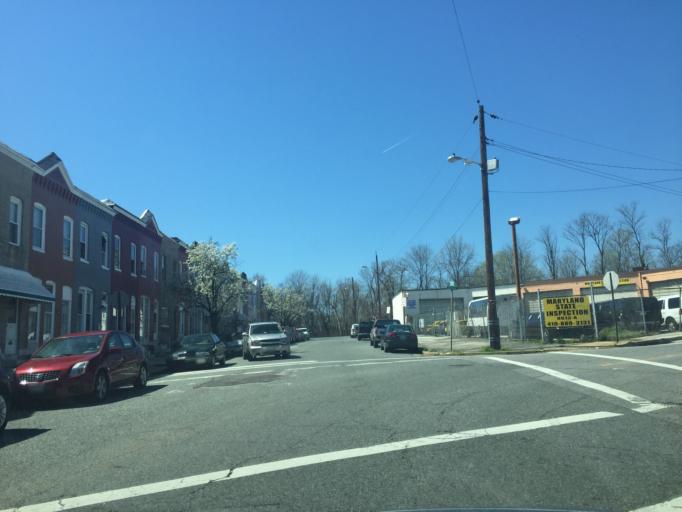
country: US
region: Maryland
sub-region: City of Baltimore
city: Baltimore
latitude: 39.3161
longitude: -76.6223
